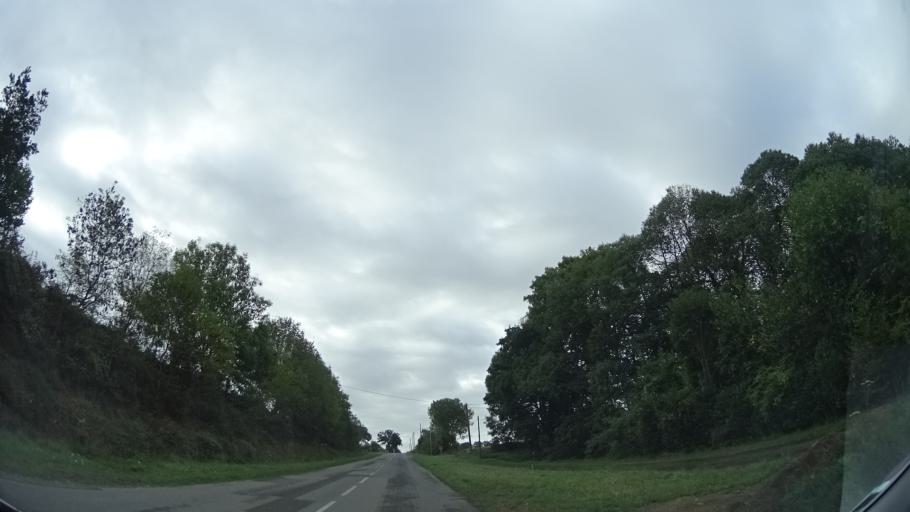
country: FR
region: Brittany
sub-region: Departement d'Ille-et-Vilaine
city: Montreuil-sur-Ille
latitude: 48.3361
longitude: -1.6491
